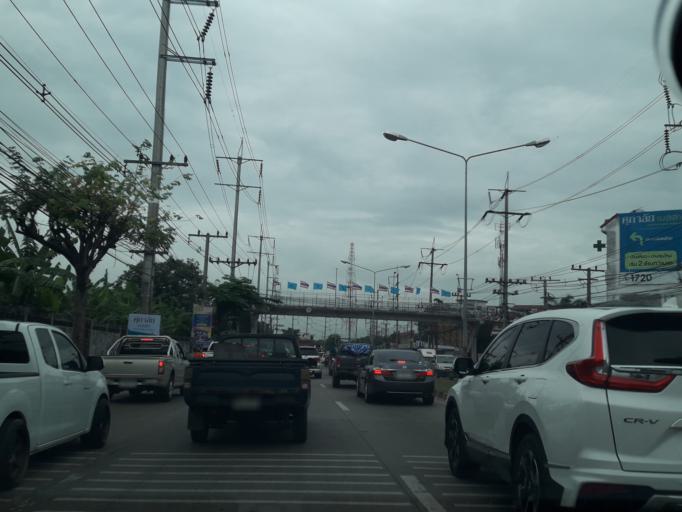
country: TH
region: Pathum Thani
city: Lam Luk Ka
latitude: 13.9370
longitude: 100.7525
